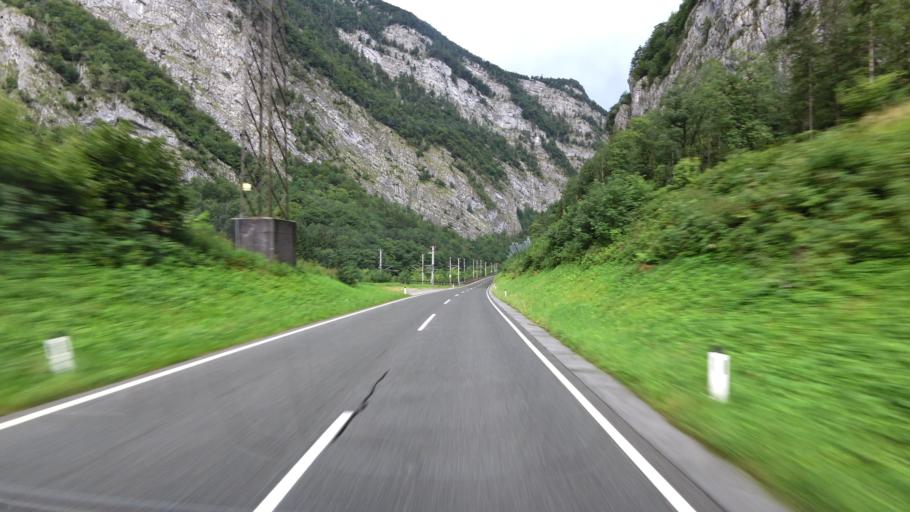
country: AT
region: Salzburg
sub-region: Politischer Bezirk Hallein
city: Golling an der Salzach
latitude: 47.5573
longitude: 13.1666
